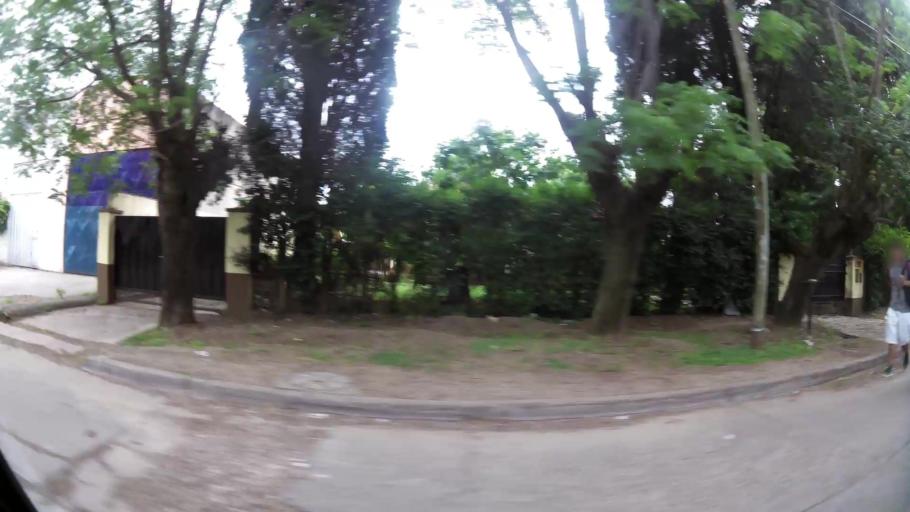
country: AR
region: Buenos Aires
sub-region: Partido de Ezeiza
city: Ezeiza
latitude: -34.8635
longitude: -58.5157
